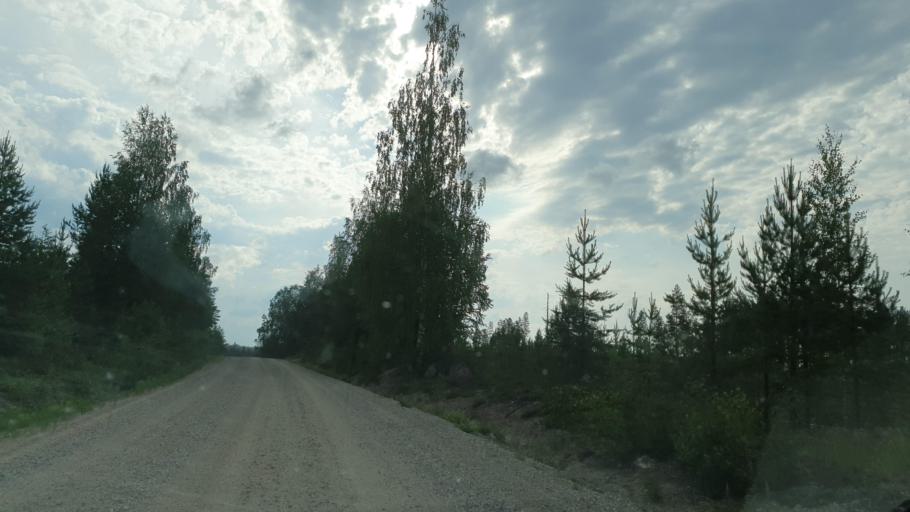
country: FI
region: Kainuu
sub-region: Kehys-Kainuu
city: Kuhmo
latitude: 64.0575
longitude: 29.8007
